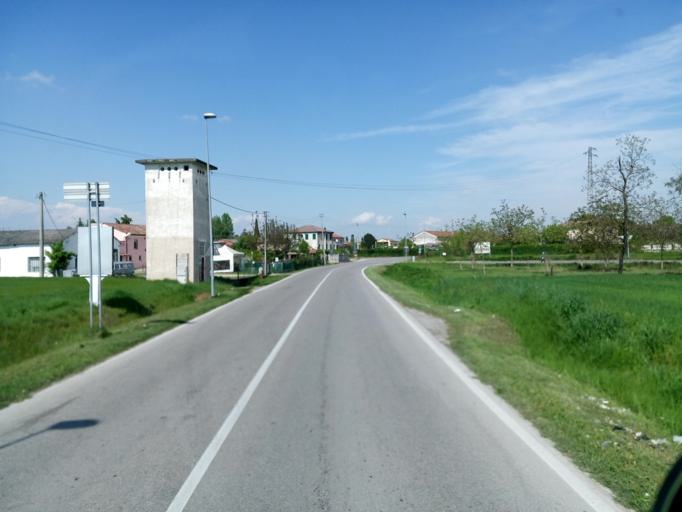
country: IT
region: Veneto
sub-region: Provincia di Verona
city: Cerea
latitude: 45.1973
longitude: 11.1956
